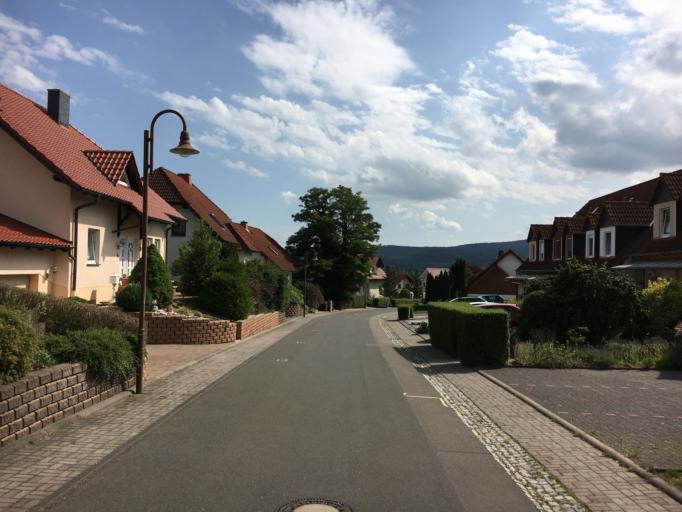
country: DE
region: Thuringia
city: Breitungen
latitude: 50.7639
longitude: 10.3344
